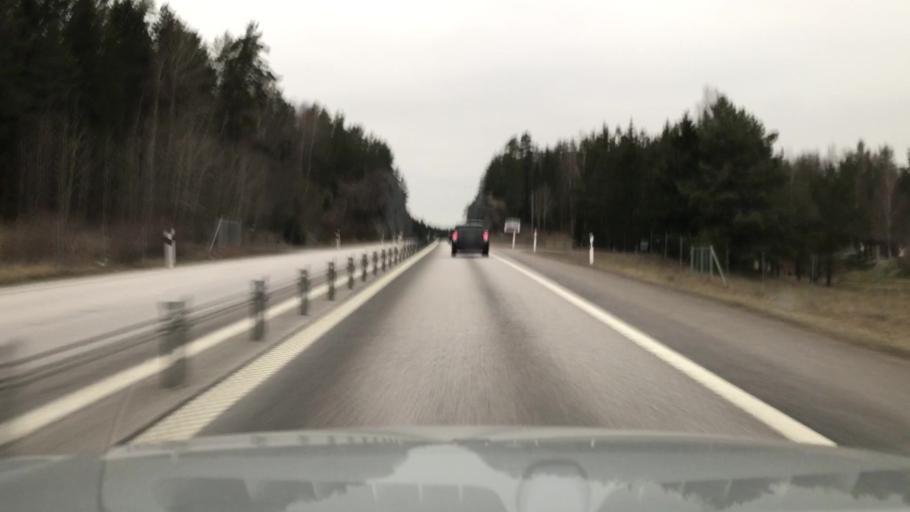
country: SE
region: OEstergoetland
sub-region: Valdemarsviks Kommun
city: Gusum
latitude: 58.2516
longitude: 16.5325
